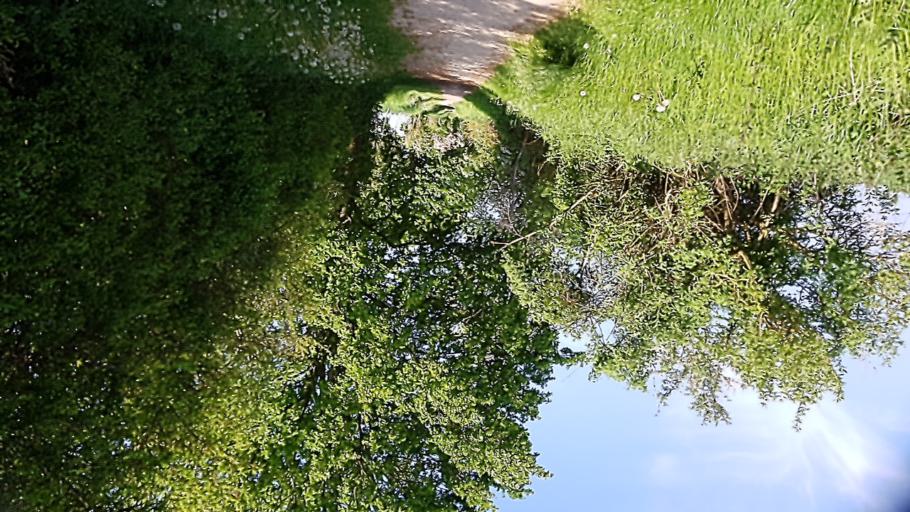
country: BE
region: Flanders
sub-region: Provincie Vlaams-Brabant
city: Huldenberg
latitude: 50.7982
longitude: 4.5747
